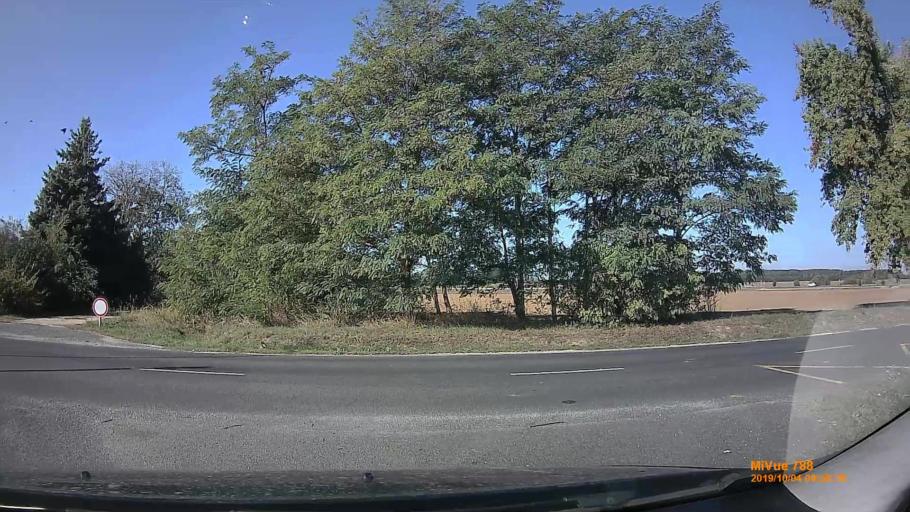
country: HU
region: Somogy
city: Kaposvar
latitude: 46.4228
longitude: 17.7756
